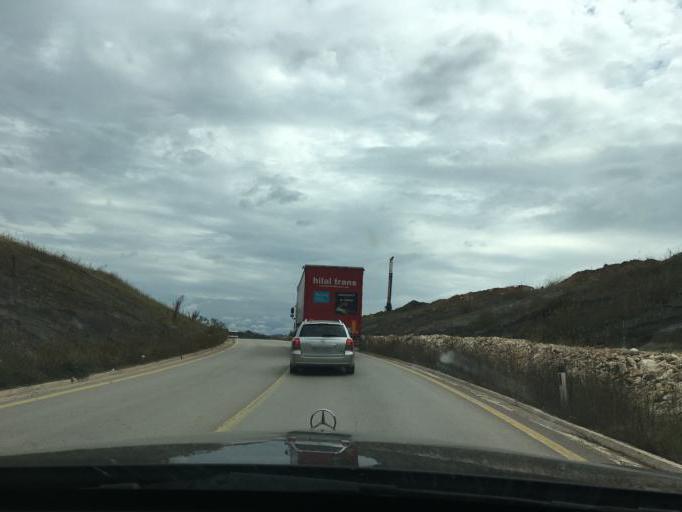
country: RS
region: Central Serbia
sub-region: Pirotski Okrug
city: Bela Palanka
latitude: 43.2613
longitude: 22.2541
